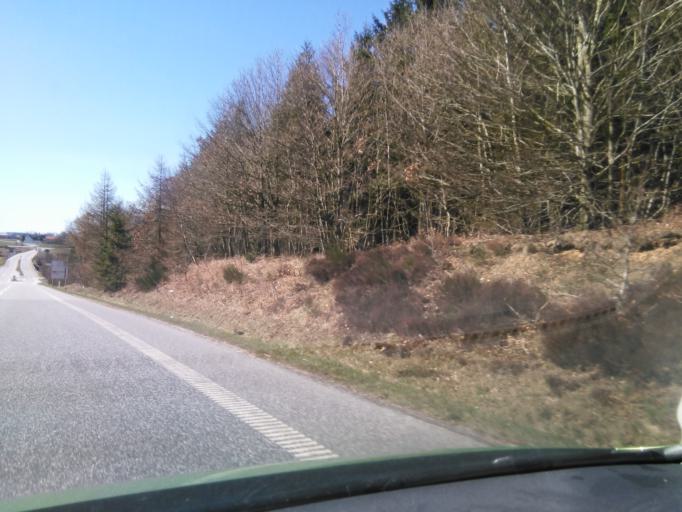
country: DK
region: Central Jutland
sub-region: Hedensted Kommune
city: Torring
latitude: 55.9705
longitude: 9.4097
